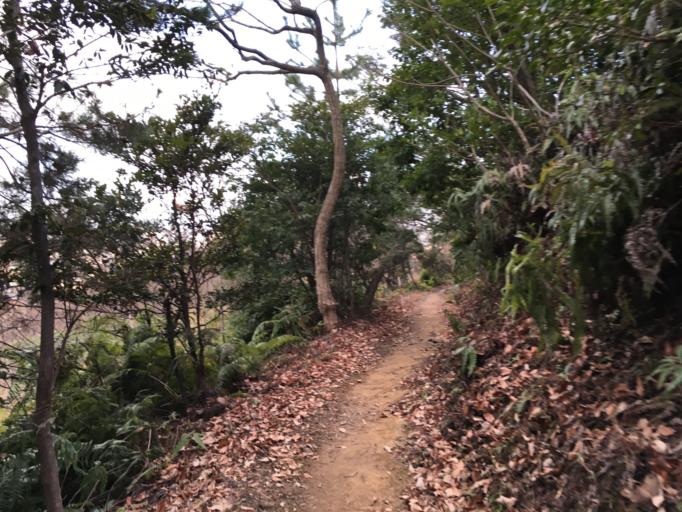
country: JP
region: Aichi
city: Toyohashi
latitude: 34.7337
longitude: 137.4462
